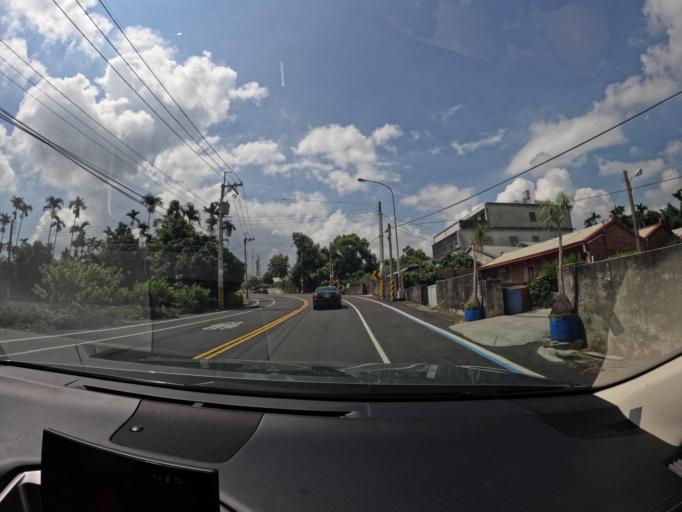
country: TW
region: Taiwan
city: Zhongxing New Village
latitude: 23.9658
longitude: 120.6276
